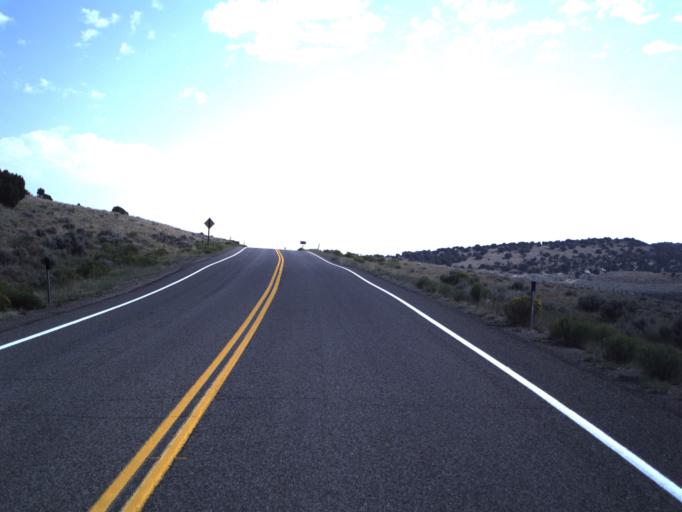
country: US
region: Utah
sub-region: Daggett County
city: Manila
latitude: 40.9316
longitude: -109.7049
